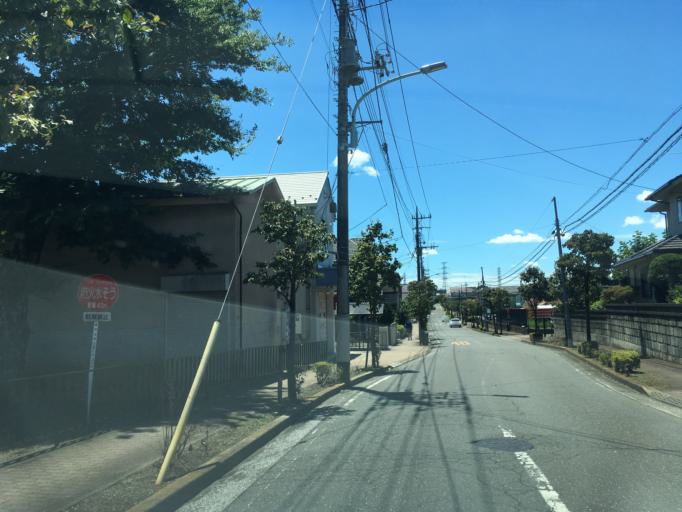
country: JP
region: Tokyo
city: Higashimurayama-shi
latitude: 35.7580
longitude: 139.4495
